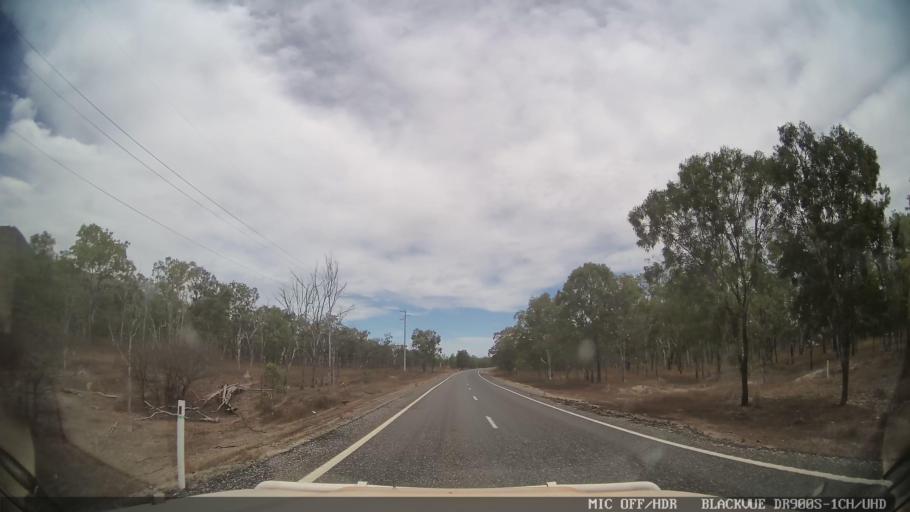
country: AU
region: Queensland
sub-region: Cairns
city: Port Douglas
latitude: -16.2498
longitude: 144.7262
